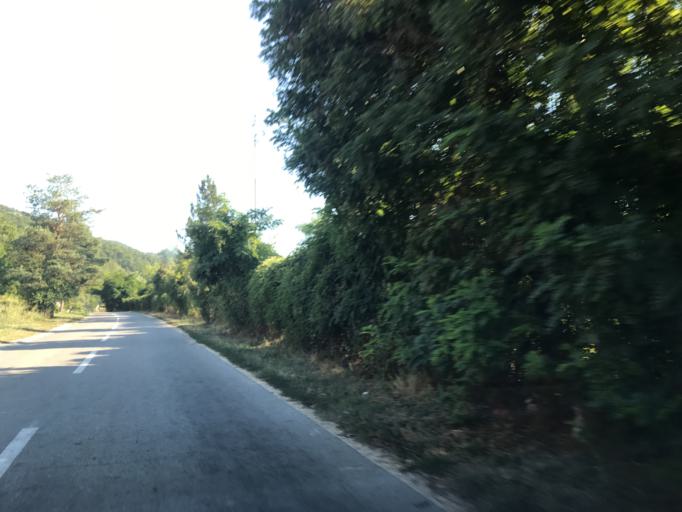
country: RO
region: Mehedinti
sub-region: Comuna Svinita
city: Svinita
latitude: 44.4258
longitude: 22.1742
